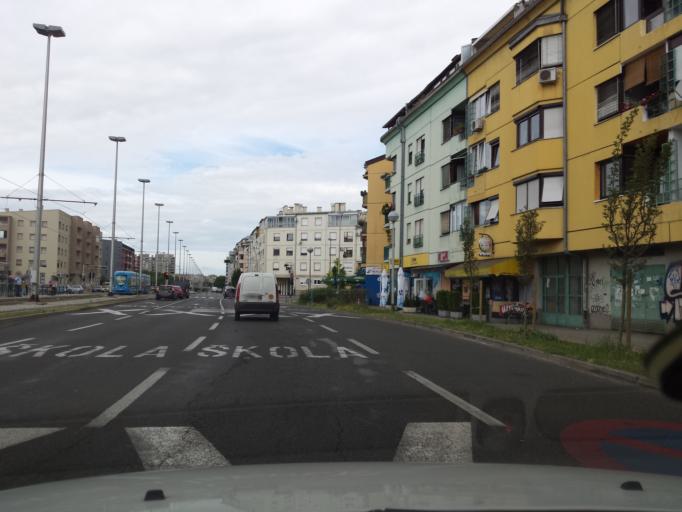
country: HR
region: Grad Zagreb
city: Jankomir
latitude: 45.7917
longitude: 15.9152
